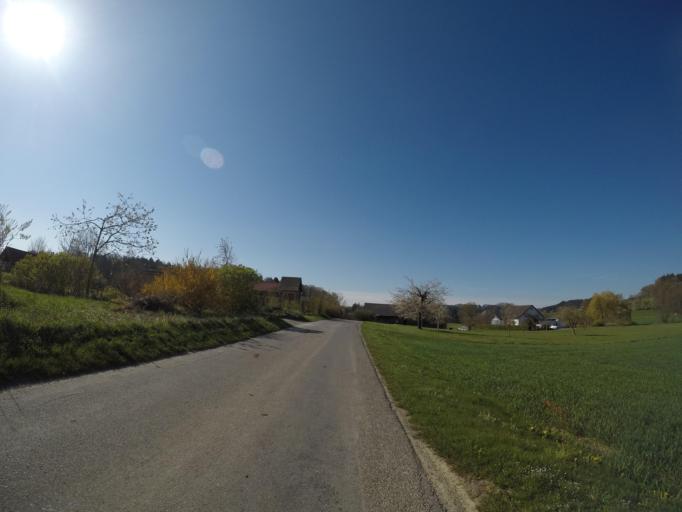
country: DE
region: Baden-Wuerttemberg
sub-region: Tuebingen Region
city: Ebenweiler
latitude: 47.8903
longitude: 9.5242
